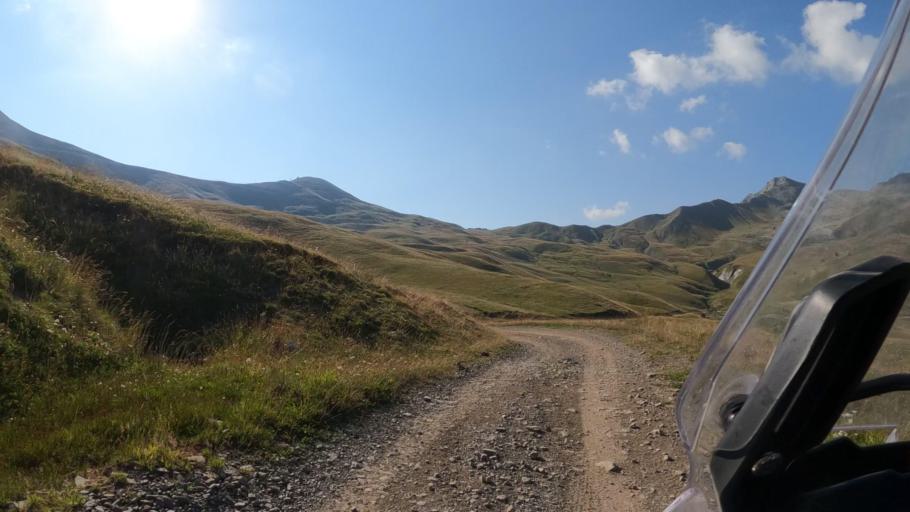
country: FR
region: Provence-Alpes-Cote d'Azur
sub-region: Departement des Hautes-Alpes
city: Guillestre
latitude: 44.5914
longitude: 6.6401
